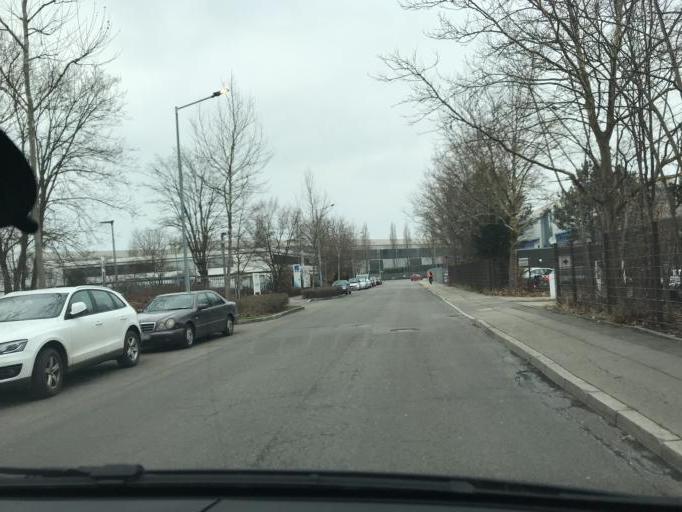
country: DE
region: Baden-Wuerttemberg
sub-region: Regierungsbezirk Stuttgart
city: Boeblingen
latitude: 48.6805
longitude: 8.9751
